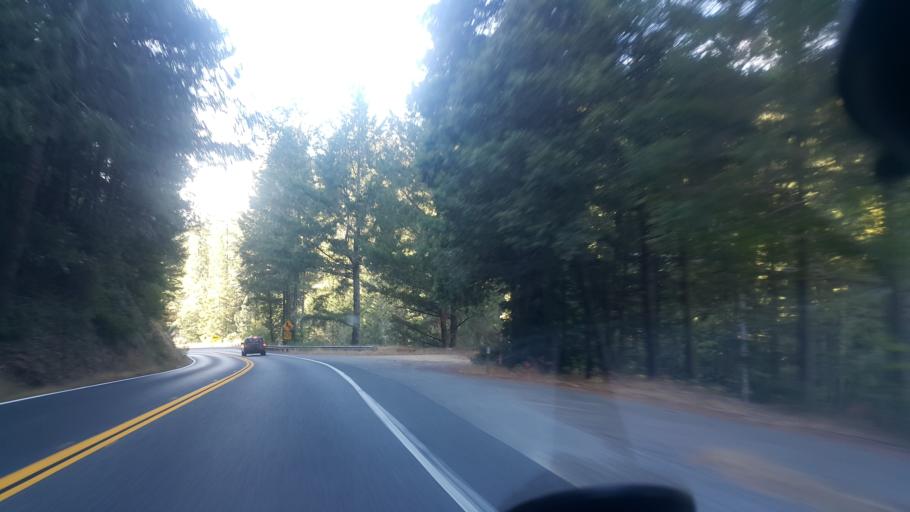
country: US
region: California
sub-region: Mendocino County
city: Brooktrails
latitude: 39.3553
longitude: -123.5099
